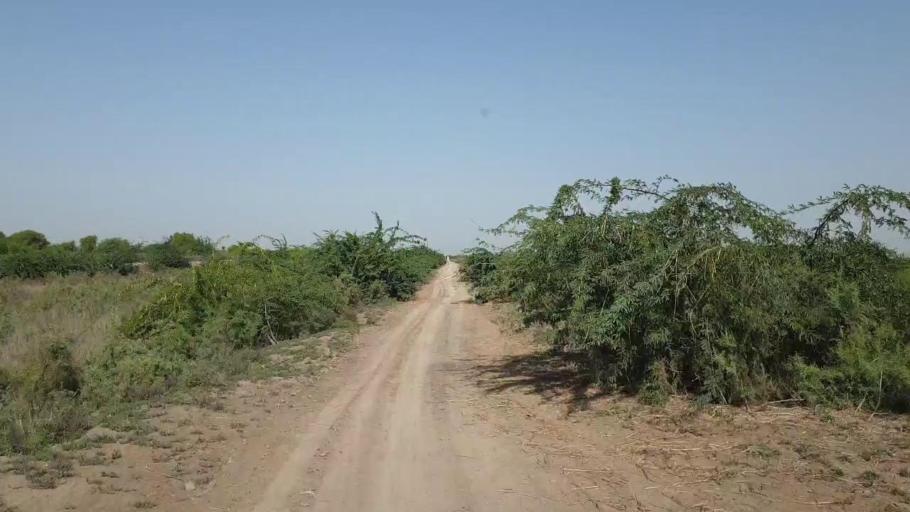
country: PK
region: Sindh
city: Tando Bago
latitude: 24.6582
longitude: 69.0697
